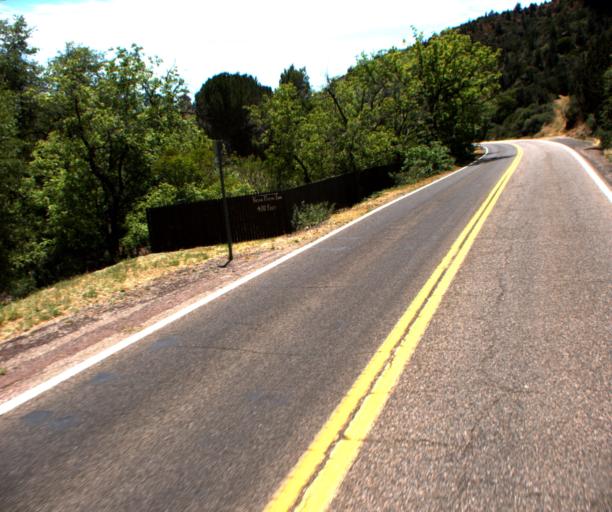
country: US
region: Arizona
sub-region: Coconino County
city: Sedona
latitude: 34.9011
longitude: -111.7303
